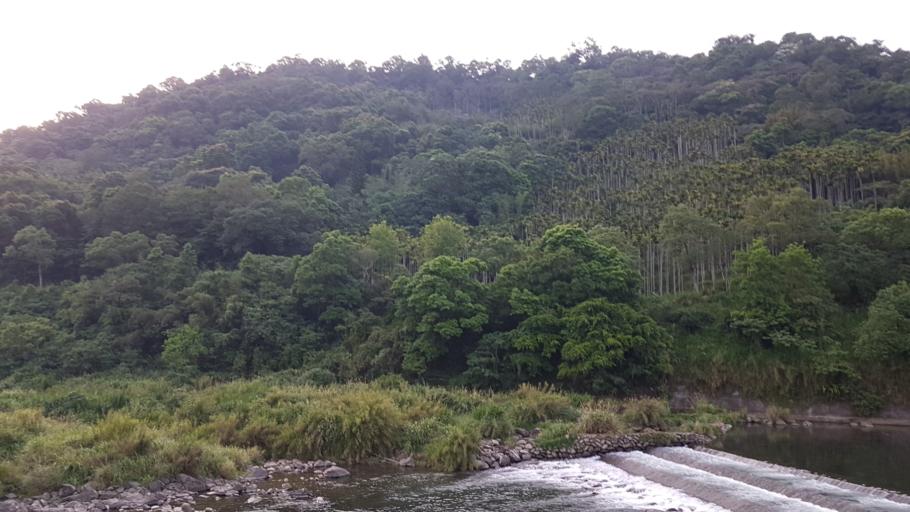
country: TW
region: Taiwan
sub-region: Yilan
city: Yilan
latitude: 24.9353
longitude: 121.6997
